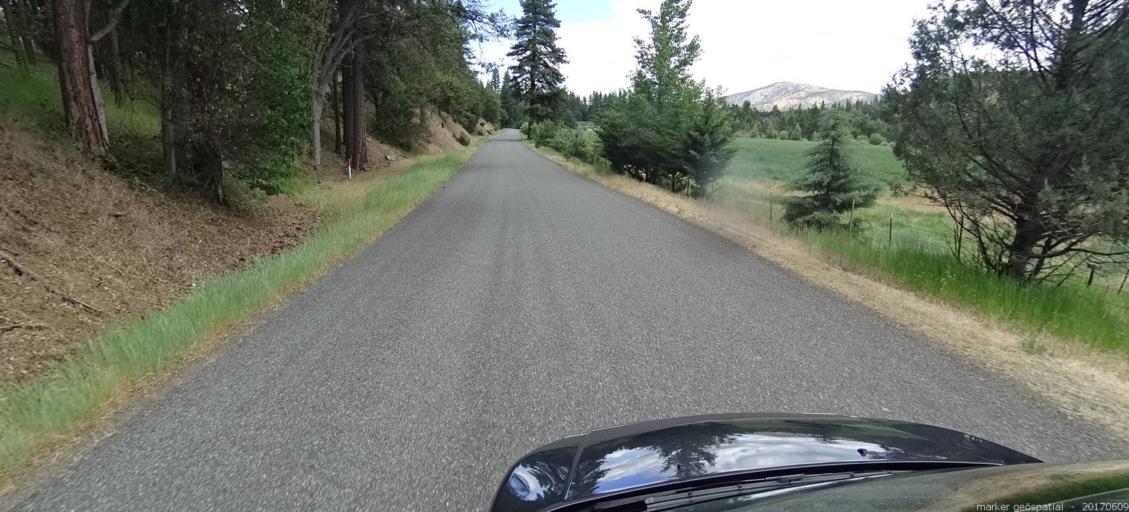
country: US
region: California
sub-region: Siskiyou County
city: Yreka
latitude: 41.3973
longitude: -122.8722
